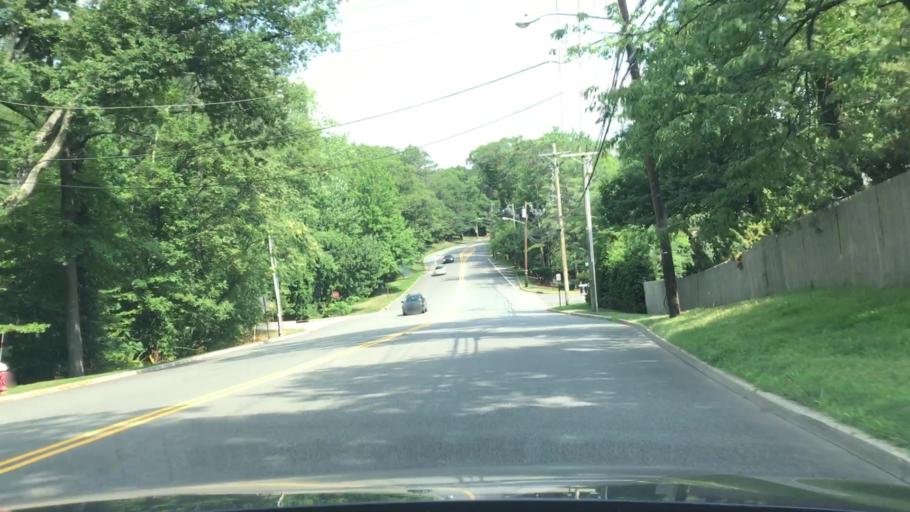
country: US
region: New Jersey
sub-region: Bergen County
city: Tenafly
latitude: 40.9123
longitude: -73.9476
